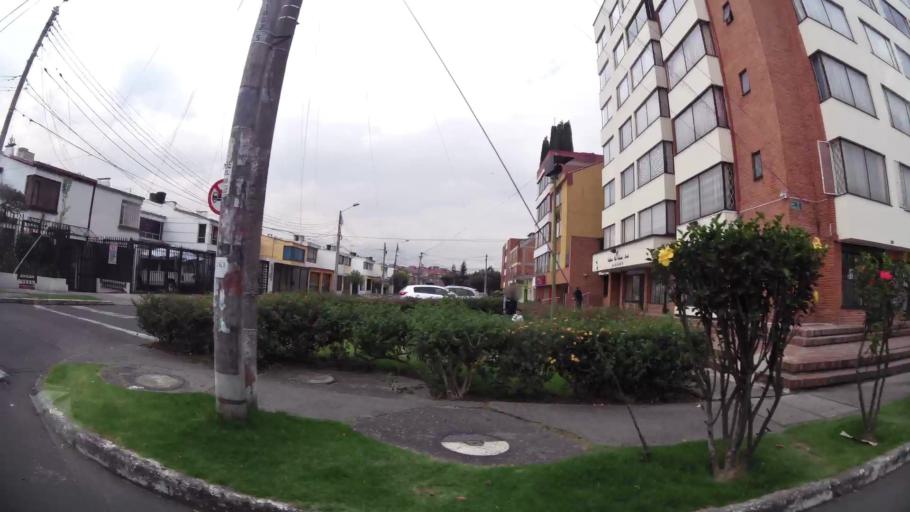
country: CO
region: Bogota D.C.
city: Barrio San Luis
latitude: 4.6865
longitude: -74.0688
